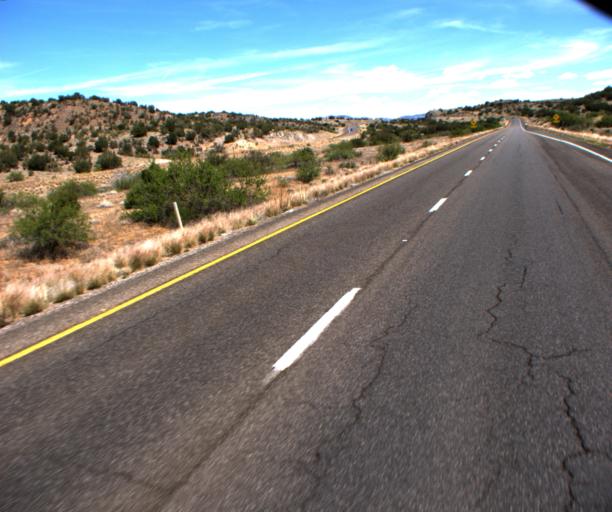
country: US
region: Arizona
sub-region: Yavapai County
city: Cornville
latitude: 34.7955
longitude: -111.9152
